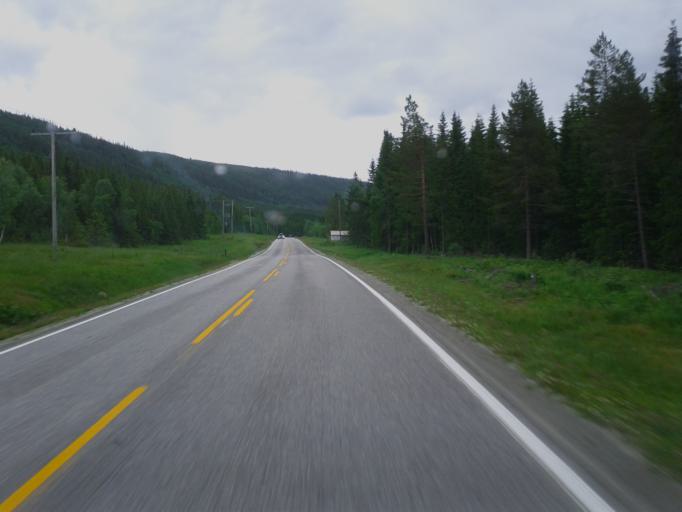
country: NO
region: Nord-Trondelag
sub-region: Namsskogan
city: Namsskogan
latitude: 64.8782
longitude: 13.0670
